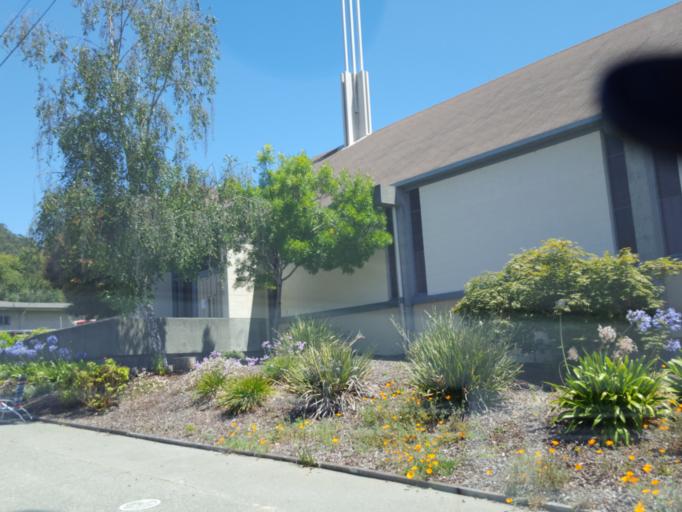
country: US
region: California
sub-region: Contra Costa County
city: El Cerrito
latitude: 37.9173
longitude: -122.3031
